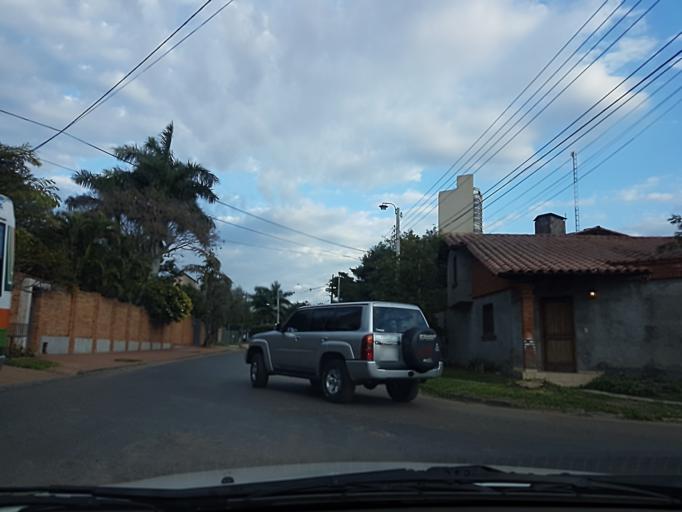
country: PY
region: Central
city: Fernando de la Mora
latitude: -25.2903
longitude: -57.5516
